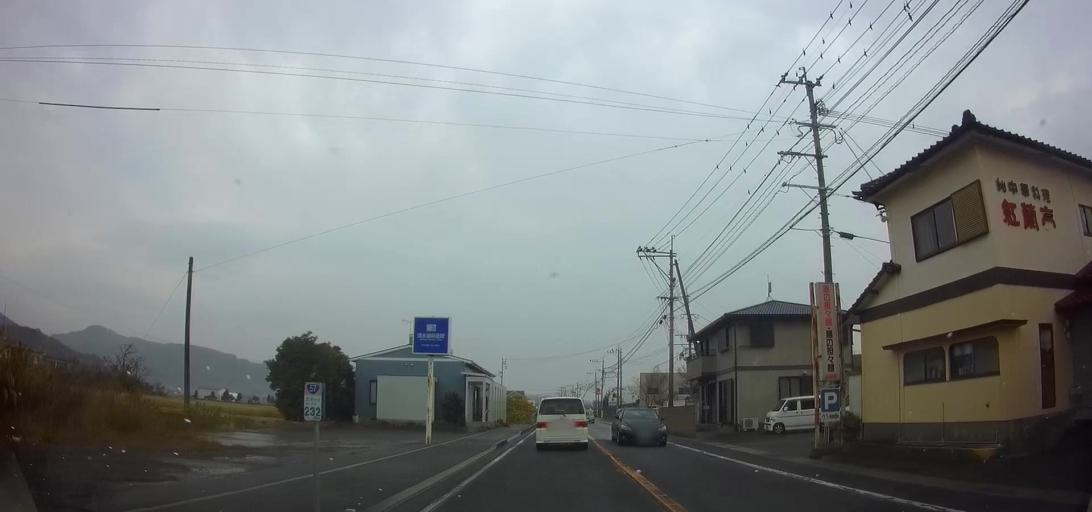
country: JP
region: Nagasaki
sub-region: Isahaya-shi
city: Isahaya
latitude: 32.8342
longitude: 130.1308
